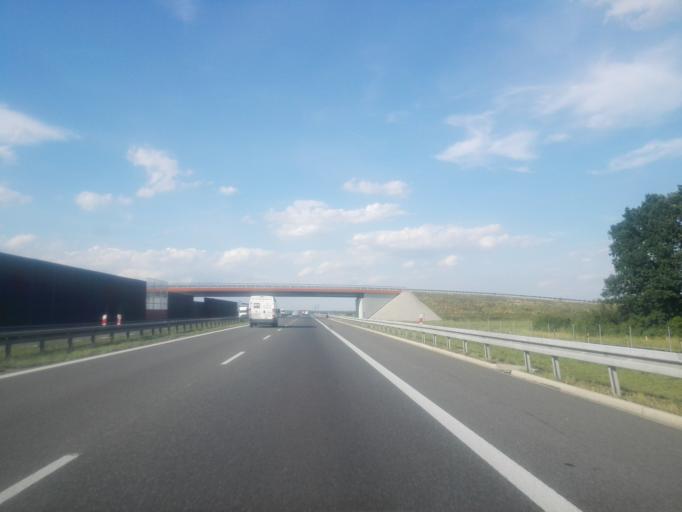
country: PL
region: Lower Silesian Voivodeship
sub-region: Powiat wroclawski
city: Mirkow
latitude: 51.1913
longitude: 17.1115
